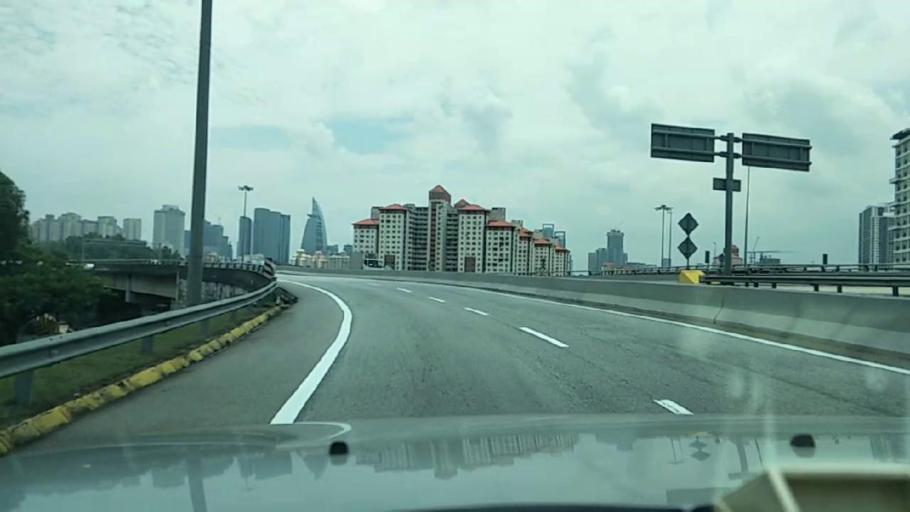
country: MY
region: Kuala Lumpur
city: Kuala Lumpur
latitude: 3.0921
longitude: 101.6713
